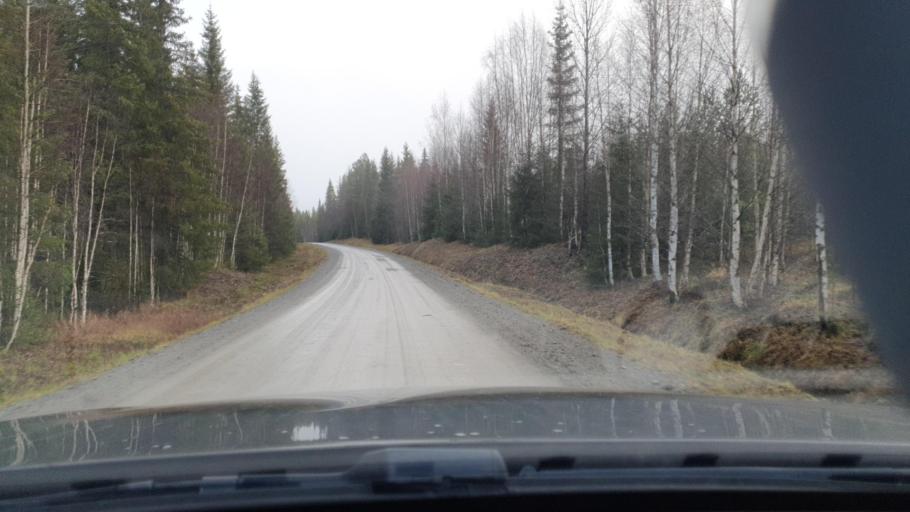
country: SE
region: Jaemtland
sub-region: Stroemsunds Kommun
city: Stroemsund
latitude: 63.5444
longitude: 15.5635
